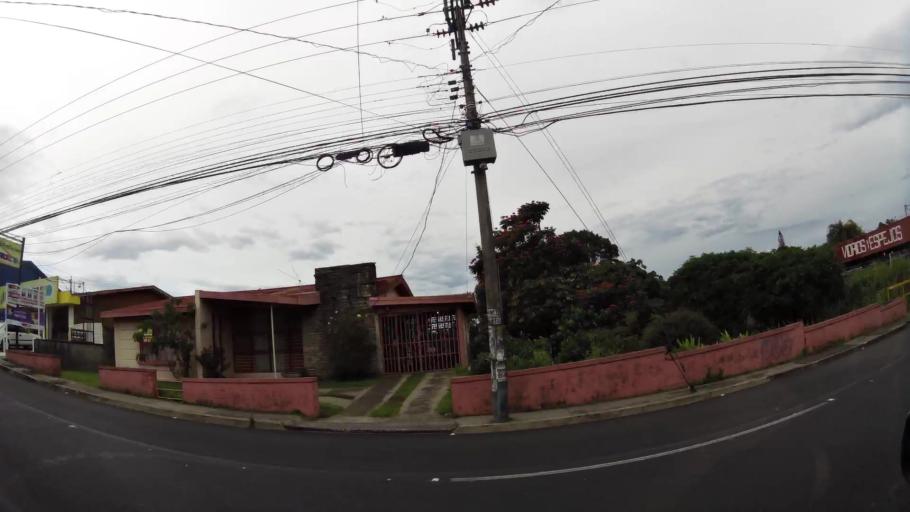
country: CR
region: San Jose
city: San Vicente
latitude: 9.9546
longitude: -84.0483
